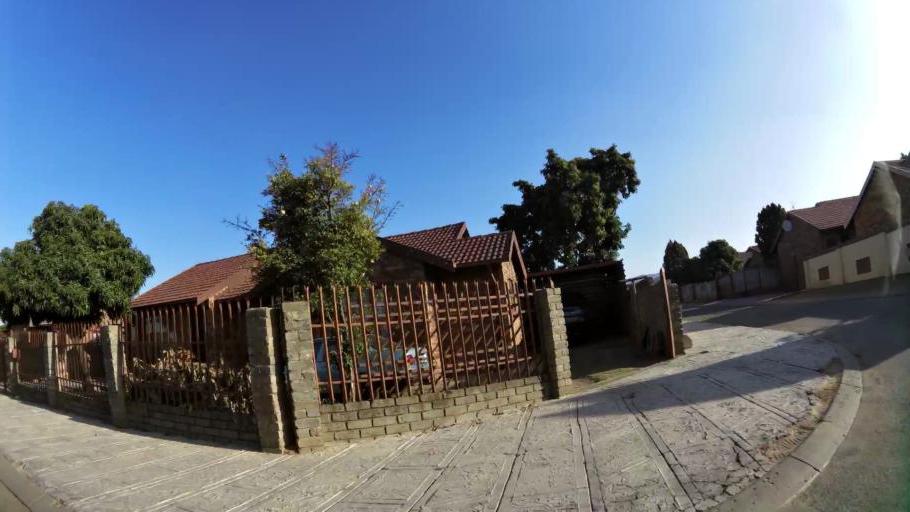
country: ZA
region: North-West
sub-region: Bojanala Platinum District Municipality
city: Rustenburg
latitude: -25.6482
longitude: 27.2215
